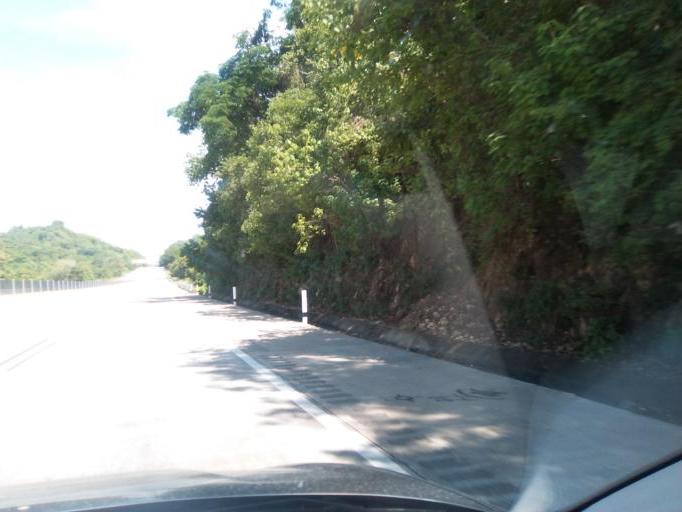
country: MX
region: Guerrero
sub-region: Acapulco de Juarez
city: Kilometro 30
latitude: 16.9778
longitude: -99.7190
